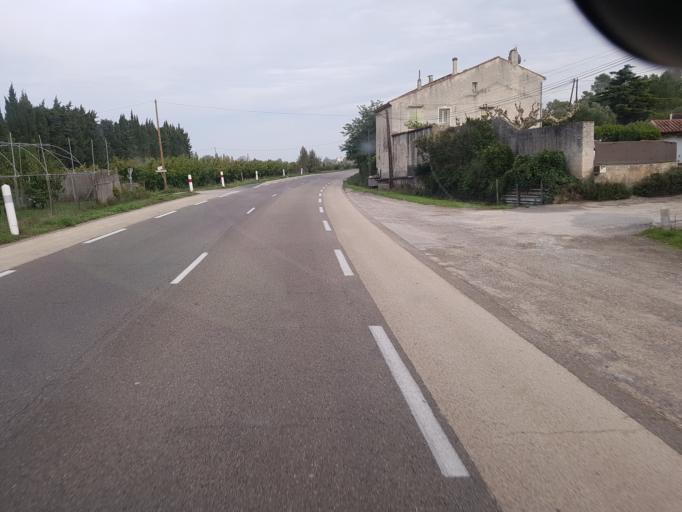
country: FR
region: Provence-Alpes-Cote d'Azur
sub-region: Departement des Bouches-du-Rhone
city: Barbentane
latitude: 43.8994
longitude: 4.7233
